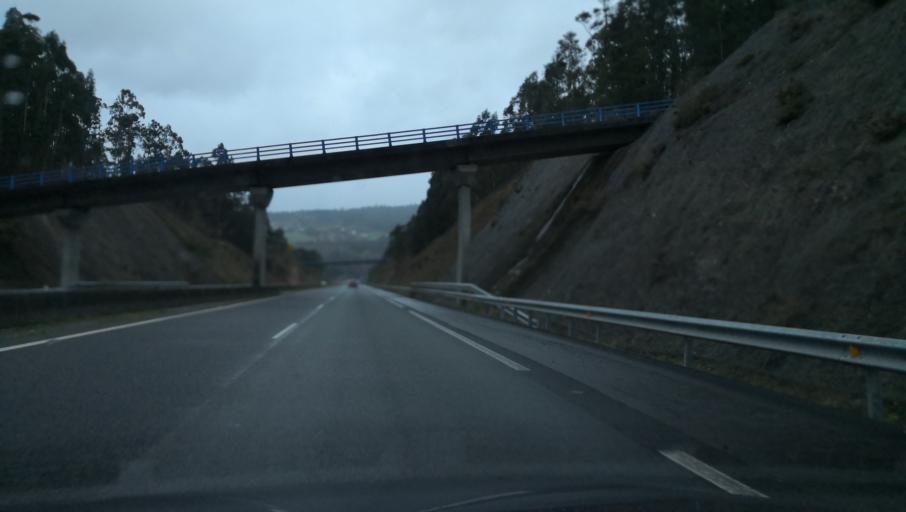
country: ES
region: Galicia
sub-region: Provincia da Coruna
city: Vedra
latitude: 42.8239
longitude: -8.5073
